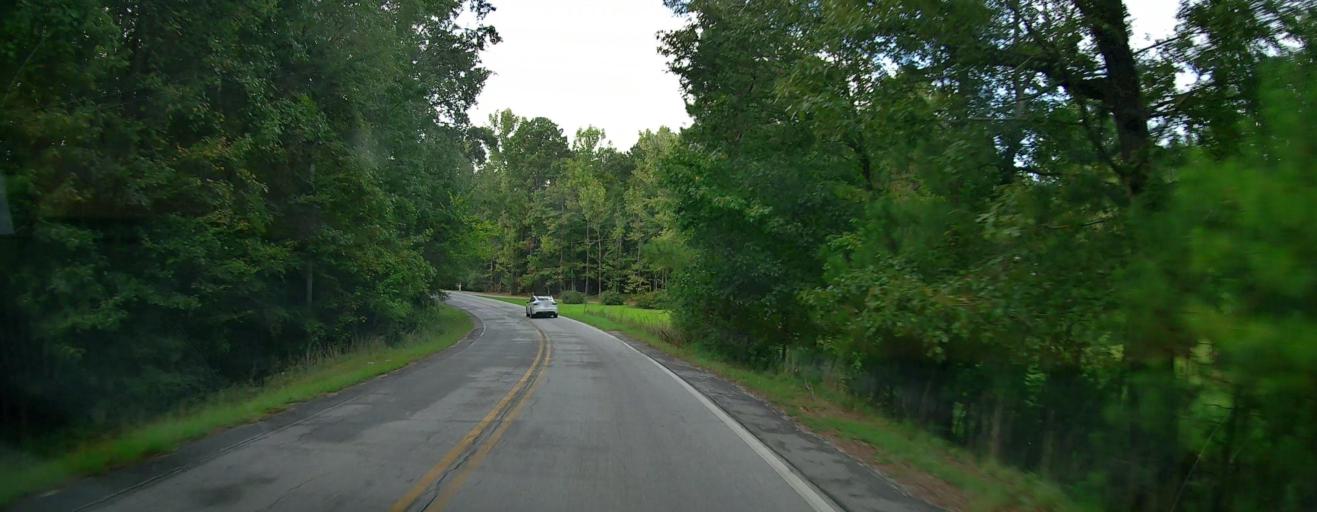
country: US
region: Alabama
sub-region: Russell County
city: Phenix City
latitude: 32.5921
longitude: -84.9373
